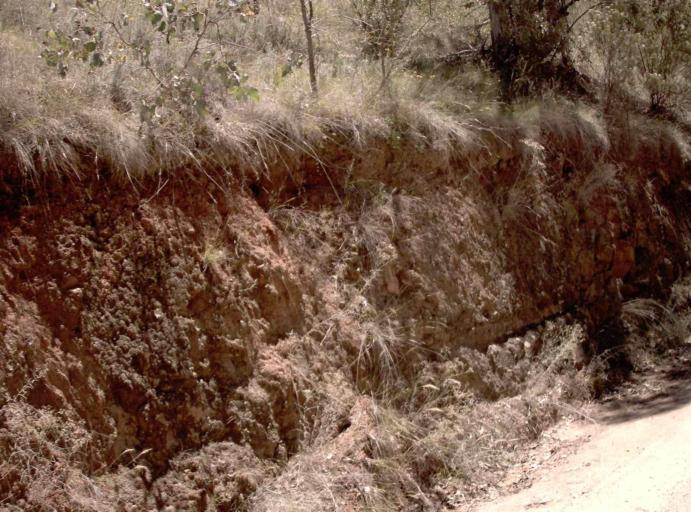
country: AU
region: New South Wales
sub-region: Snowy River
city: Jindabyne
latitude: -36.9304
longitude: 148.3683
